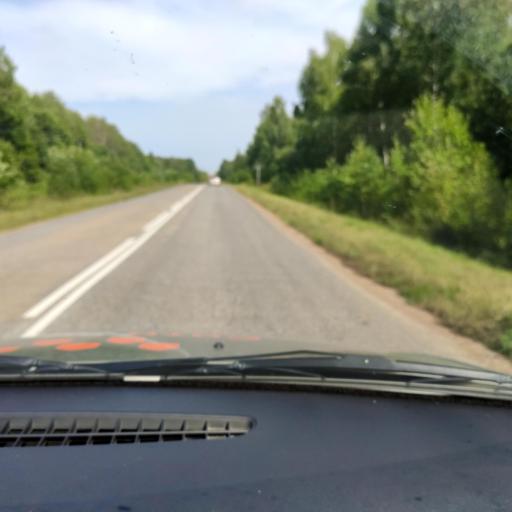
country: RU
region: Bashkortostan
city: Pavlovka
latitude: 55.3926
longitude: 56.5361
